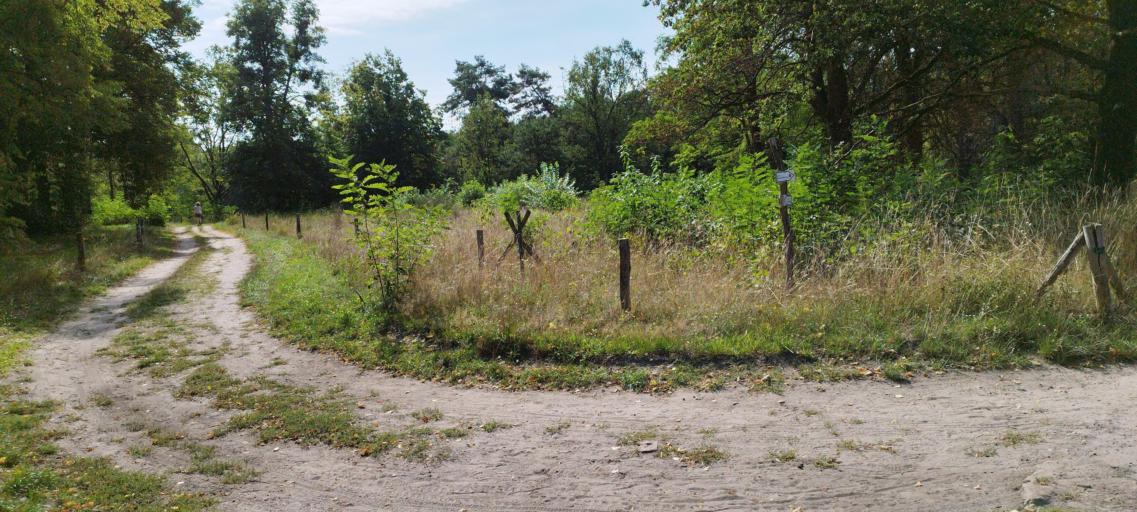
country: DE
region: Brandenburg
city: Dallgow-Doeberitz
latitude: 52.5306
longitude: 13.0535
